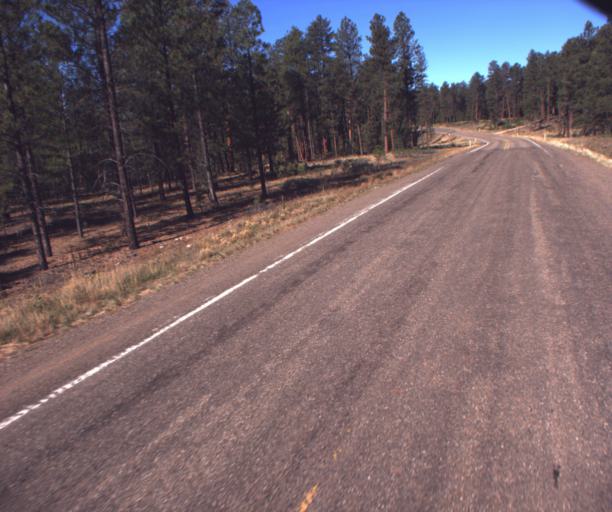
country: US
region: Arizona
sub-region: Coconino County
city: Fredonia
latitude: 36.7469
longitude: -112.2469
